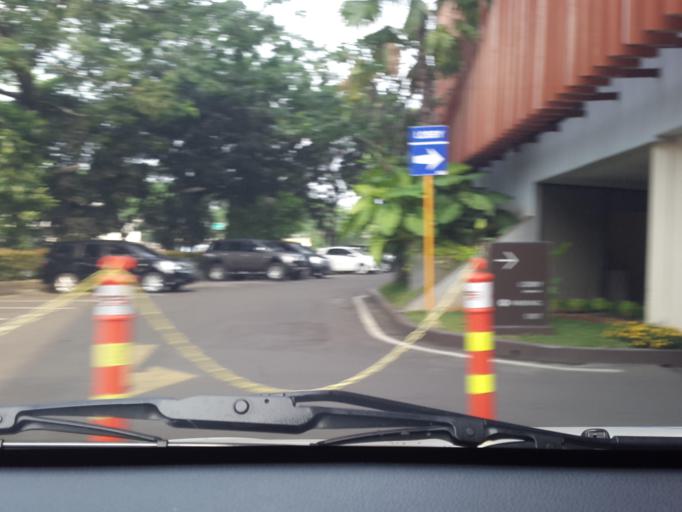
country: ID
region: Banten
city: South Tangerang
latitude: -6.2769
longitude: 106.7211
